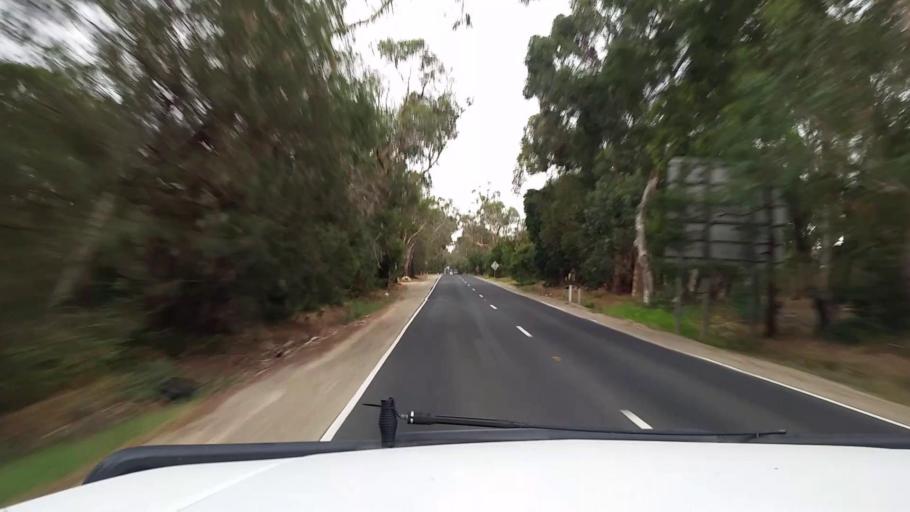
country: AU
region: Victoria
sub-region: Mornington Peninsula
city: Somerville
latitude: -38.2338
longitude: 145.1516
